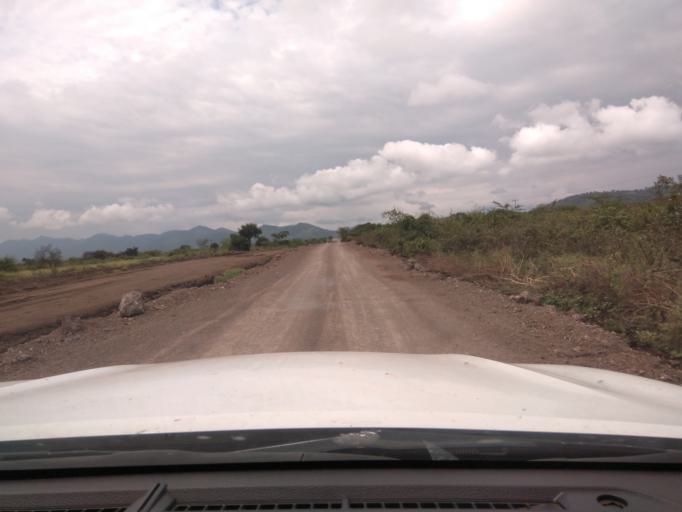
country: ET
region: Southern Nations, Nationalities, and People's Region
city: Felege Neway
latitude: 6.4026
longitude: 37.1302
